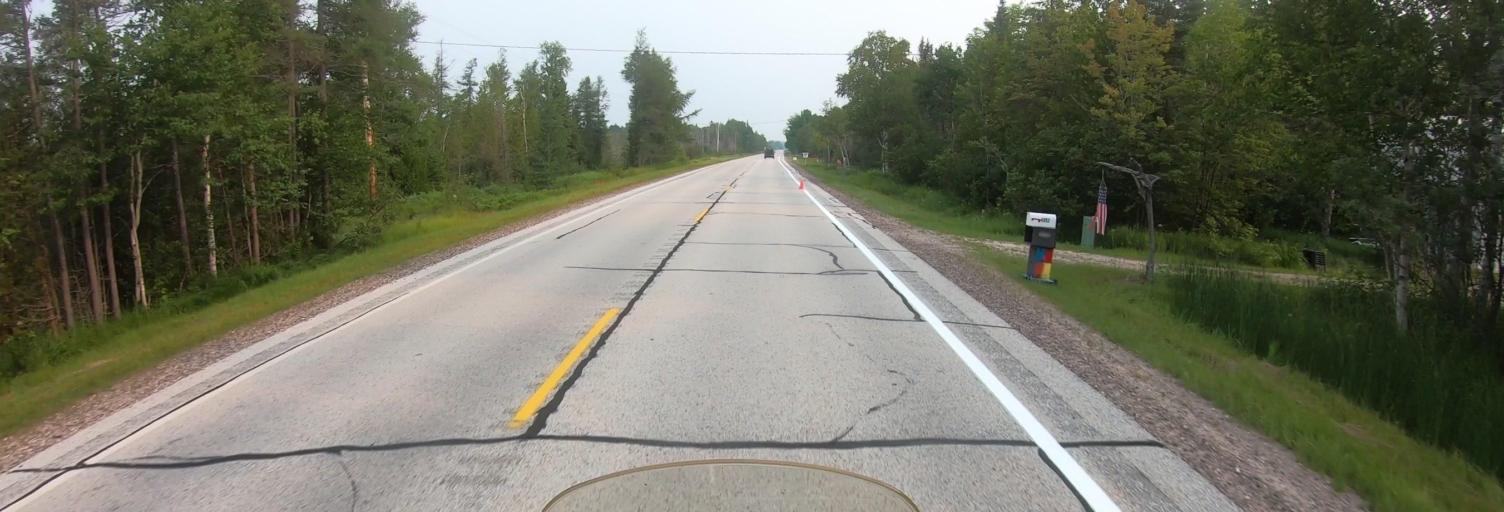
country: US
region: Michigan
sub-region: Luce County
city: Newberry
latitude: 46.5781
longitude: -85.0359
